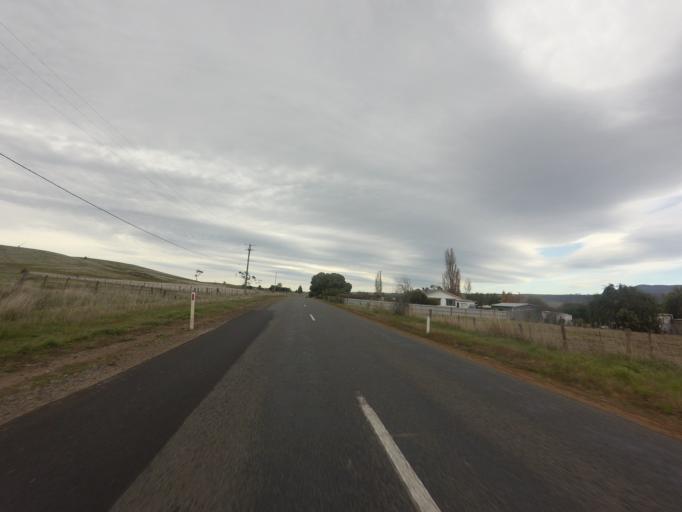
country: AU
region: Tasmania
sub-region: Derwent Valley
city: New Norfolk
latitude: -42.5087
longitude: 146.7396
